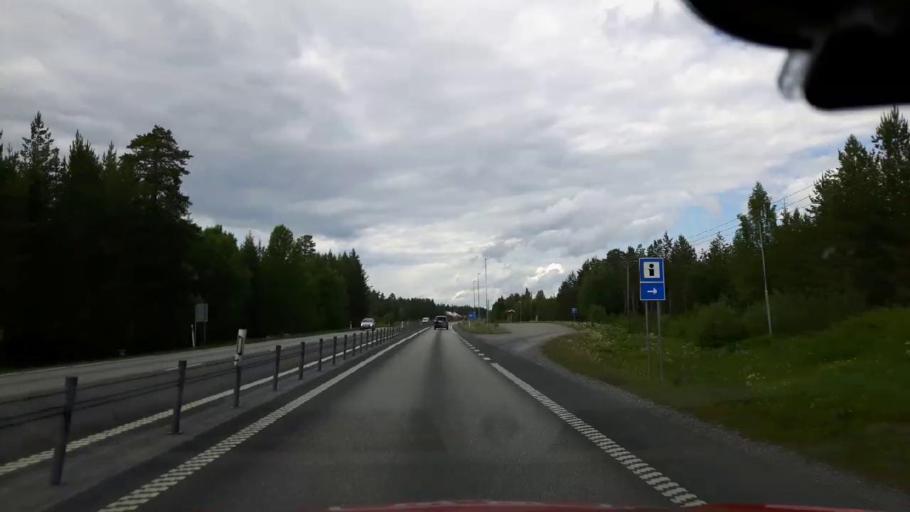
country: SE
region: Jaemtland
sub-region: OEstersunds Kommun
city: Ostersund
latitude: 63.2313
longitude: 14.6127
